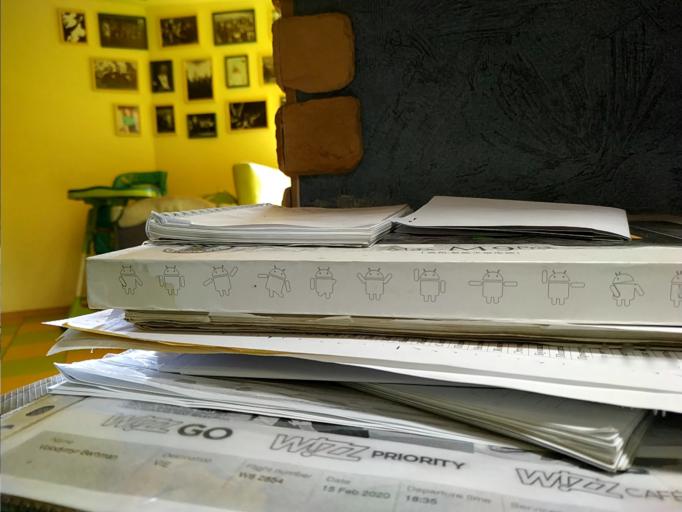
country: RU
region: Pskov
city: Plyussa
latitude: 58.5879
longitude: 29.4317
